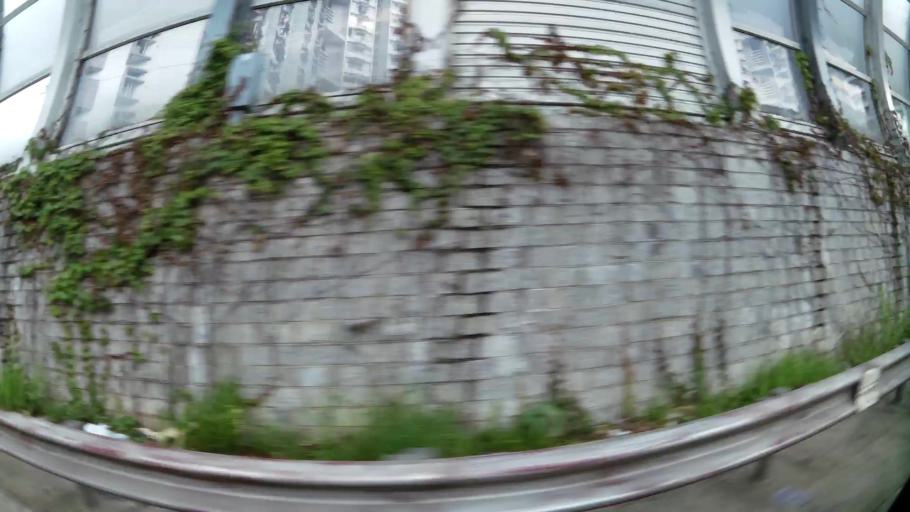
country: HK
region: Tai Po
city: Tai Po
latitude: 22.4515
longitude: 114.1585
